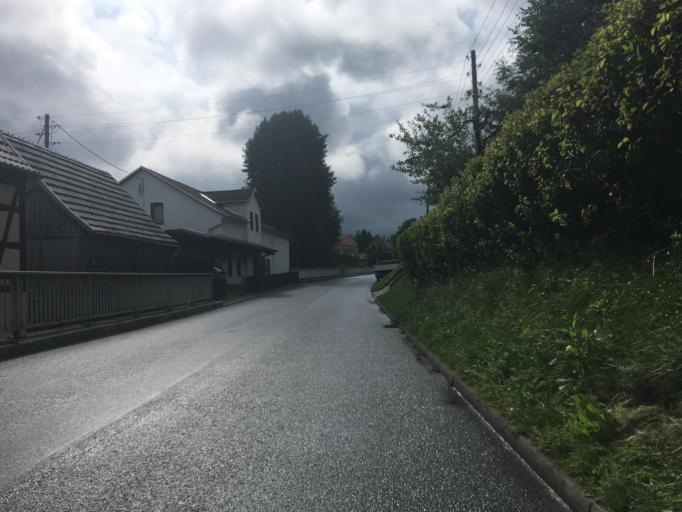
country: DE
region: Saxony
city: Bad Schandau
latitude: 50.8926
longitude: 14.1936
